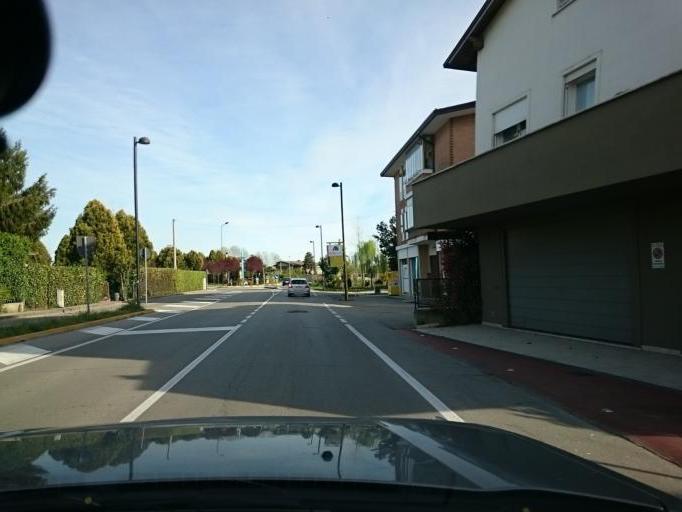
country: IT
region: Veneto
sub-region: Provincia di Padova
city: Mandriola-Sant'Agostino
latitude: 45.3719
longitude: 11.8585
